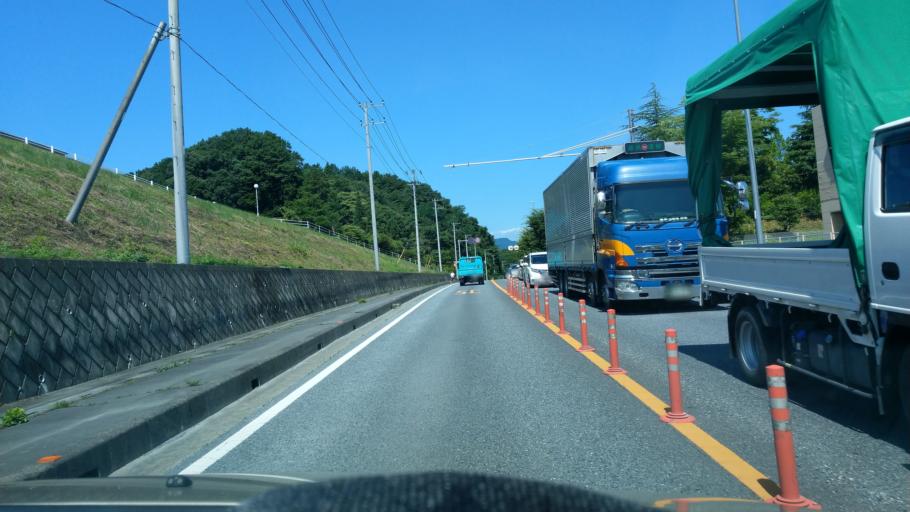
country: JP
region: Saitama
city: Ogawa
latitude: 36.0678
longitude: 139.2592
